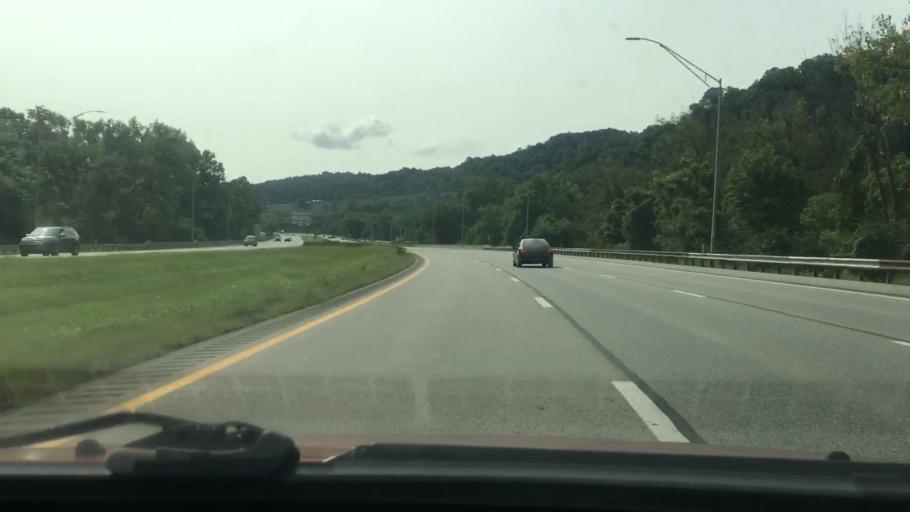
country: US
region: West Virginia
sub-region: Ohio County
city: Bethlehem
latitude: 40.0607
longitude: -80.6834
